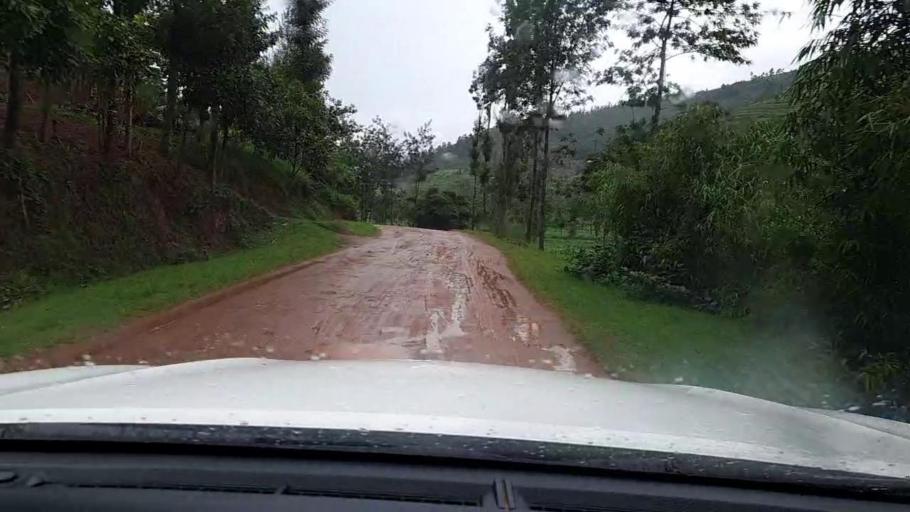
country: RW
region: Northern Province
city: Byumba
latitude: -1.7337
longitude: 29.9402
